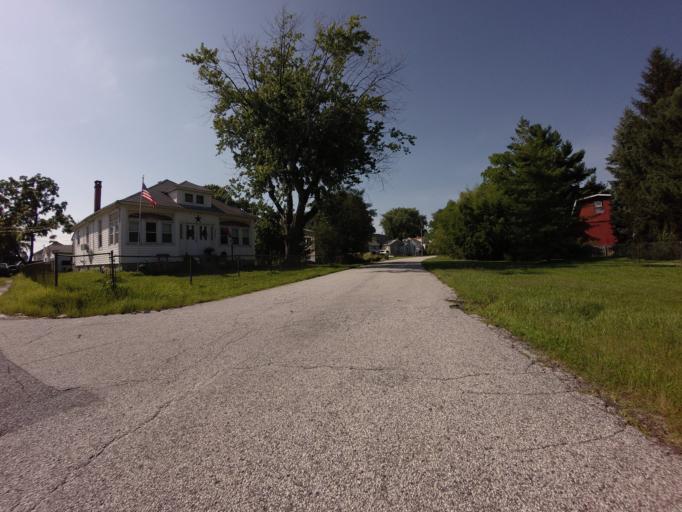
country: US
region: Maryland
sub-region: Baltimore County
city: Edgemere
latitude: 39.2048
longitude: -76.4461
